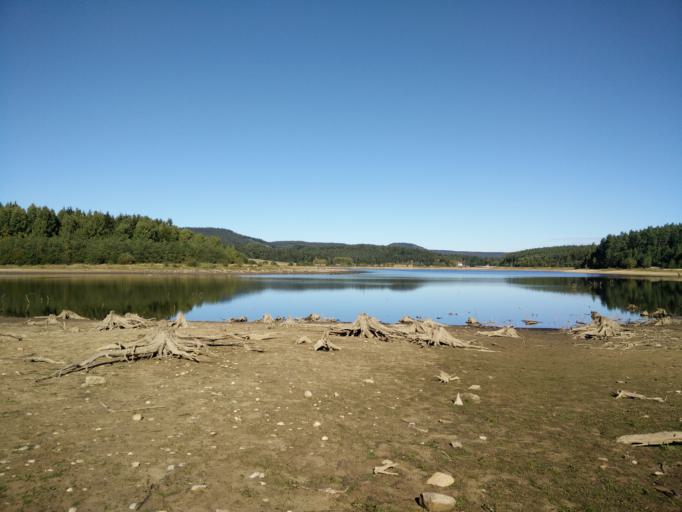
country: DE
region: Thuringia
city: Neuhaus
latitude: 50.7274
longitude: 10.9622
